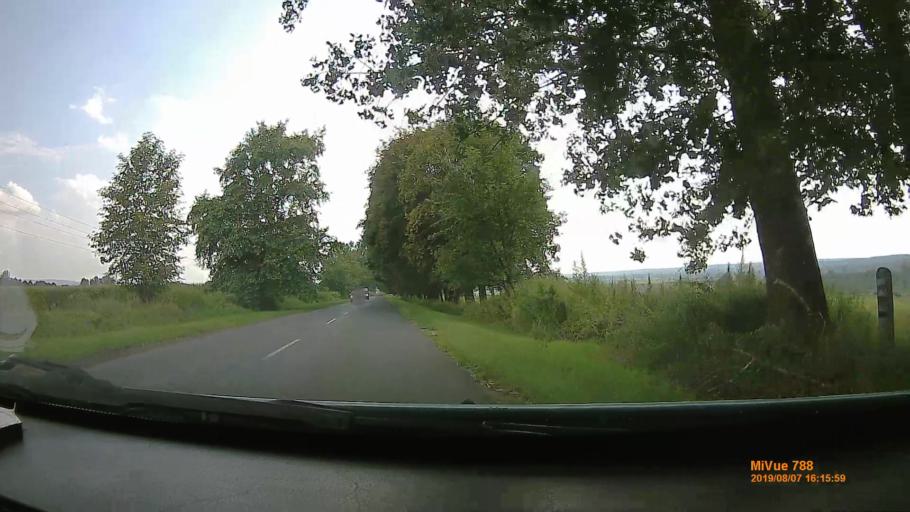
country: HU
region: Borsod-Abauj-Zemplen
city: Gonc
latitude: 48.4656
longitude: 21.2520
